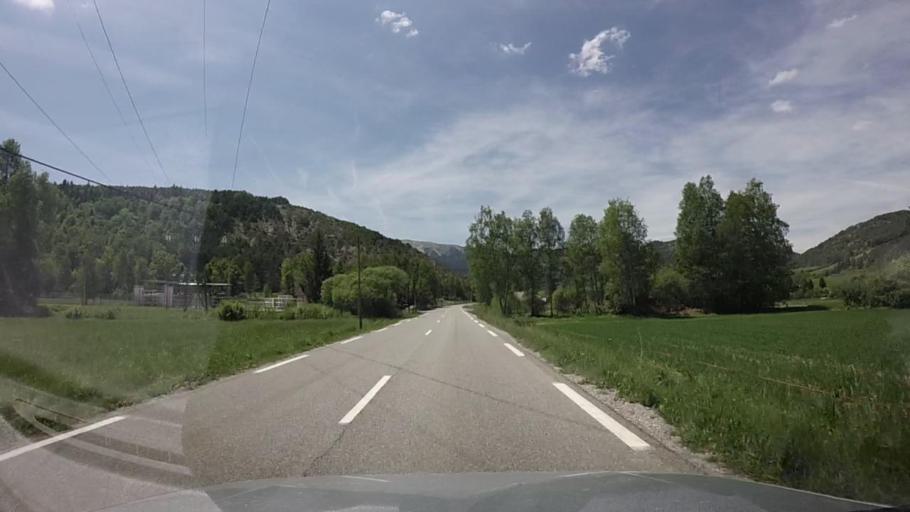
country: FR
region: Provence-Alpes-Cote d'Azur
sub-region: Departement des Alpes-de-Haute-Provence
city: Seyne-les-Alpes
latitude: 44.3769
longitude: 6.3255
